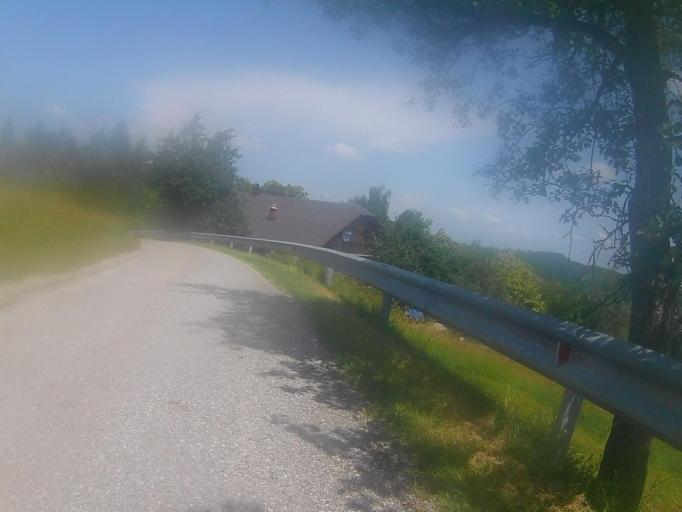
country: SI
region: Maribor
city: Bresternica
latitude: 46.6130
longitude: 15.5642
